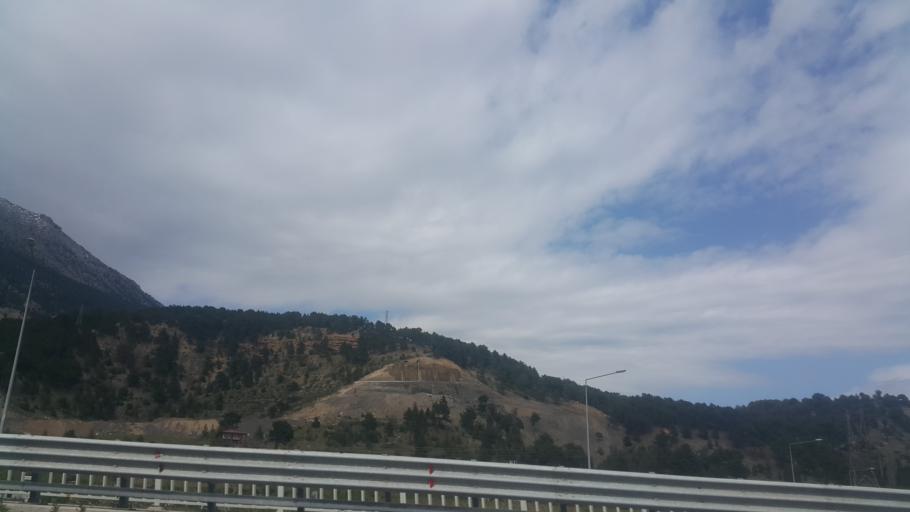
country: TR
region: Adana
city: Pozanti
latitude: 37.4632
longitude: 34.8749
